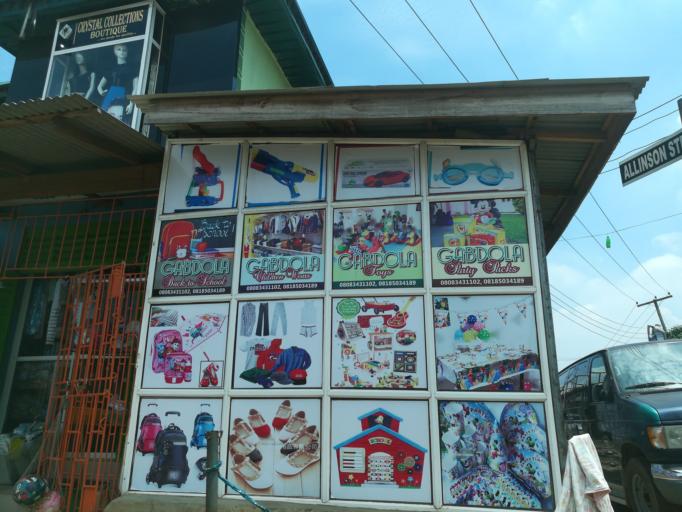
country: NG
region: Lagos
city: Ikorodu
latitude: 6.6163
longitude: 3.5015
